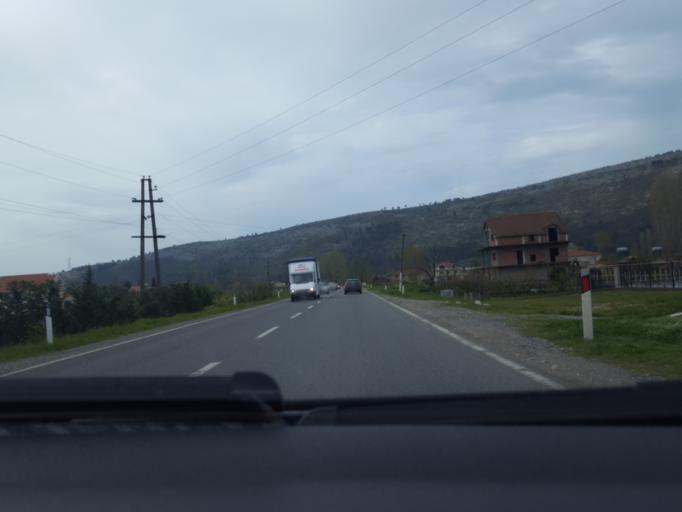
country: AL
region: Lezhe
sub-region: Rrethi i Lezhes
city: Balldreni i Ri
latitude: 41.8111
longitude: 19.6358
